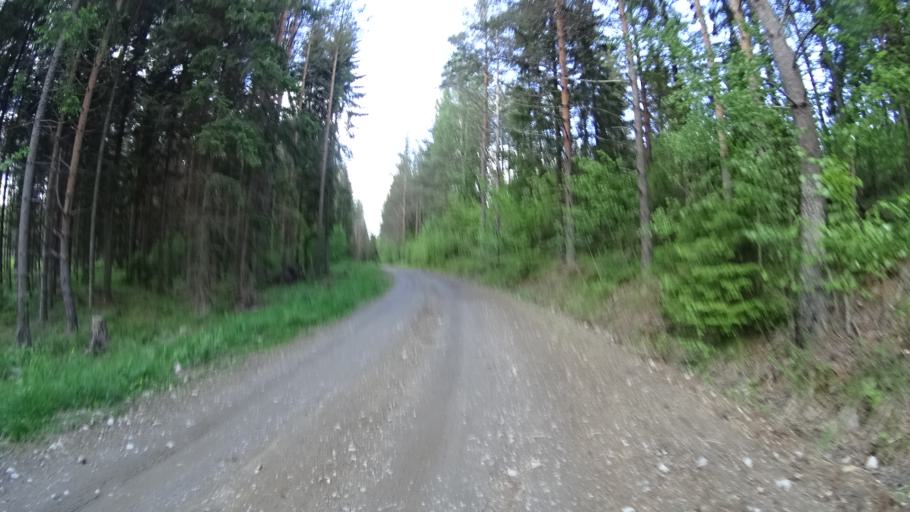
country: FI
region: Uusimaa
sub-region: Raaseporin
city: Karis
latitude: 60.1544
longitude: 23.6221
